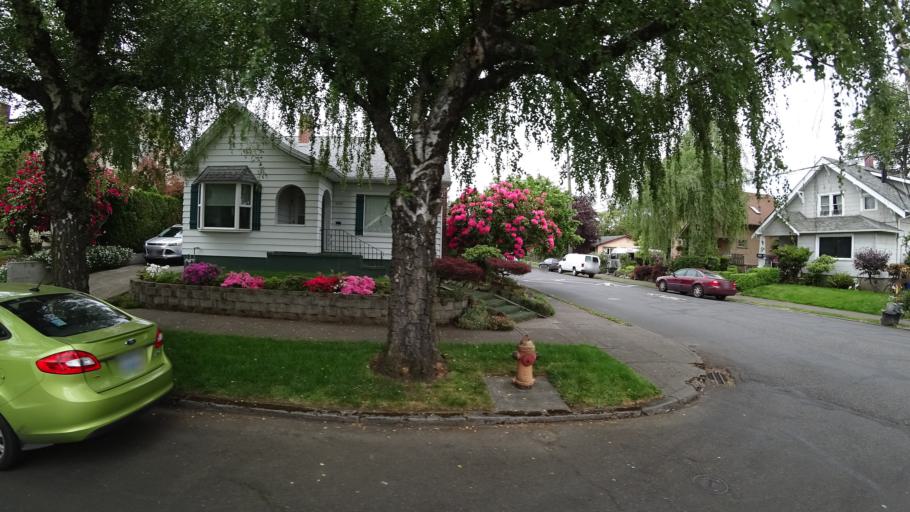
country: US
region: Oregon
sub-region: Multnomah County
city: Lents
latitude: 45.5081
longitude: -122.6172
